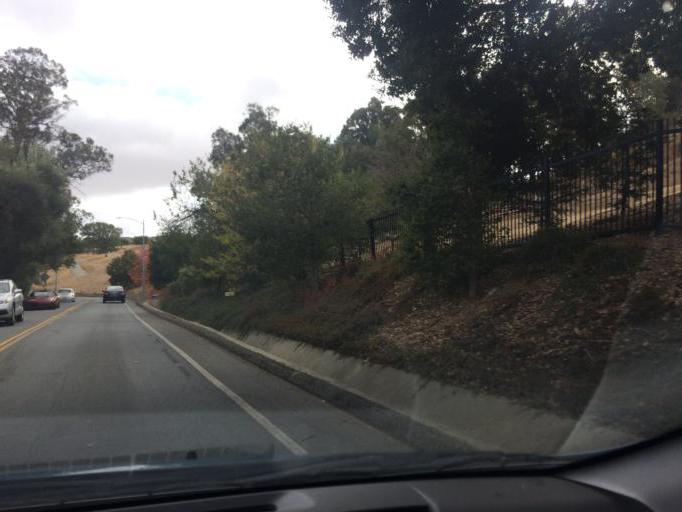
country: US
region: California
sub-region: Santa Clara County
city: Seven Trees
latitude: 37.2858
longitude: -121.7631
